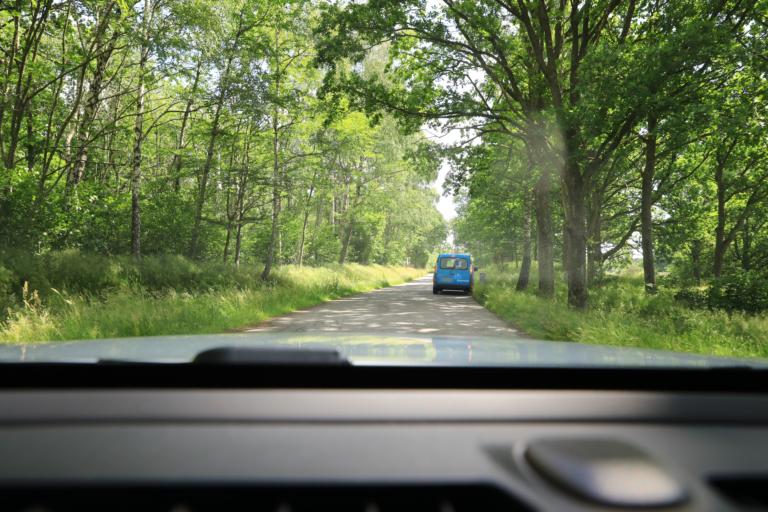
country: SE
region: Halland
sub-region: Varbergs Kommun
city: Tvaaker
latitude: 57.1060
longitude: 12.4497
